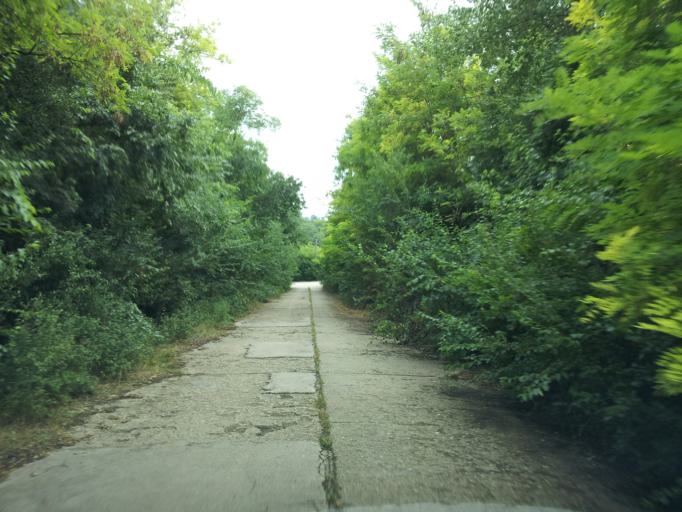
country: HU
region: Fejer
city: Enying
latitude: 46.9159
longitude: 18.2284
